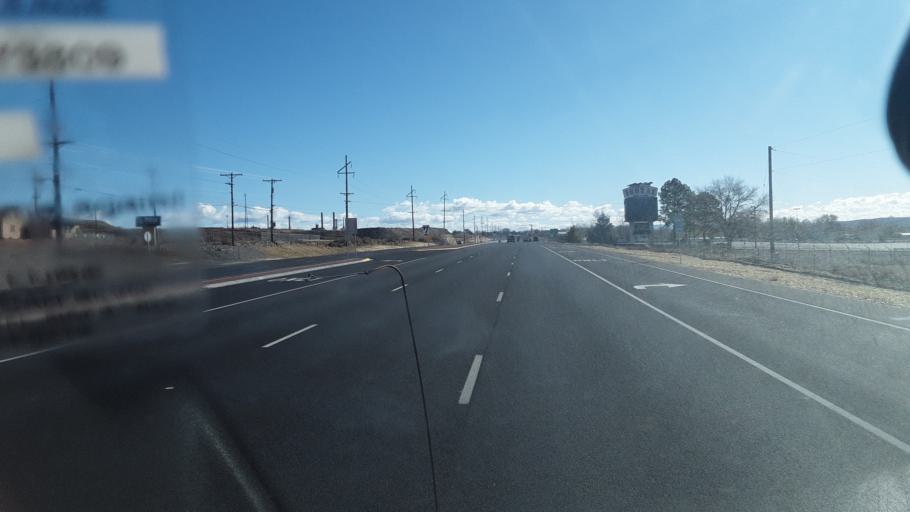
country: US
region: New Mexico
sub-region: San Juan County
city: Lee Acres
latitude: 36.7031
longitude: -108.0999
